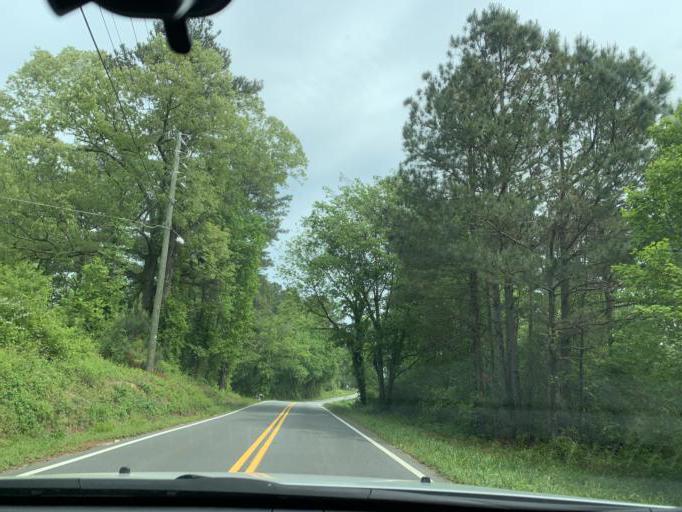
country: US
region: Georgia
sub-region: Forsyth County
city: Cumming
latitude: 34.1524
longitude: -84.1973
